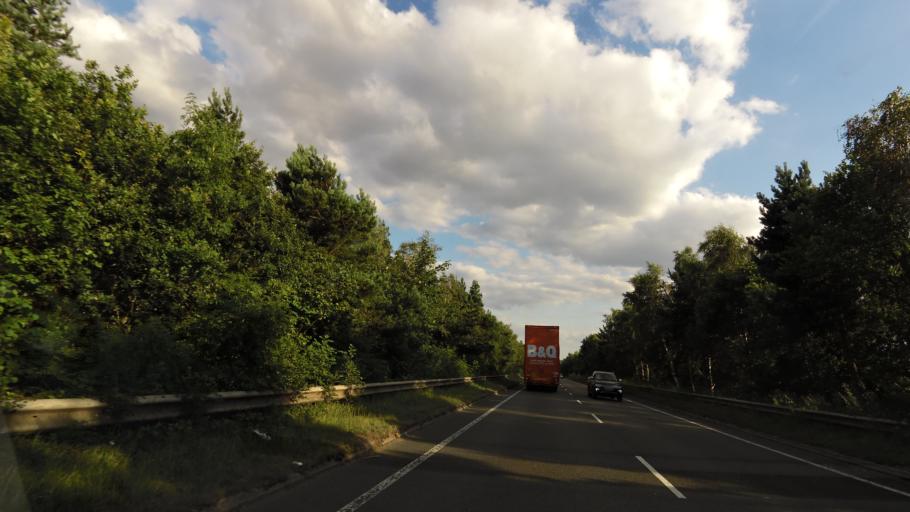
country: GB
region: England
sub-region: Rotherham
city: Woodsetts
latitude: 53.3199
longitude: -1.1531
